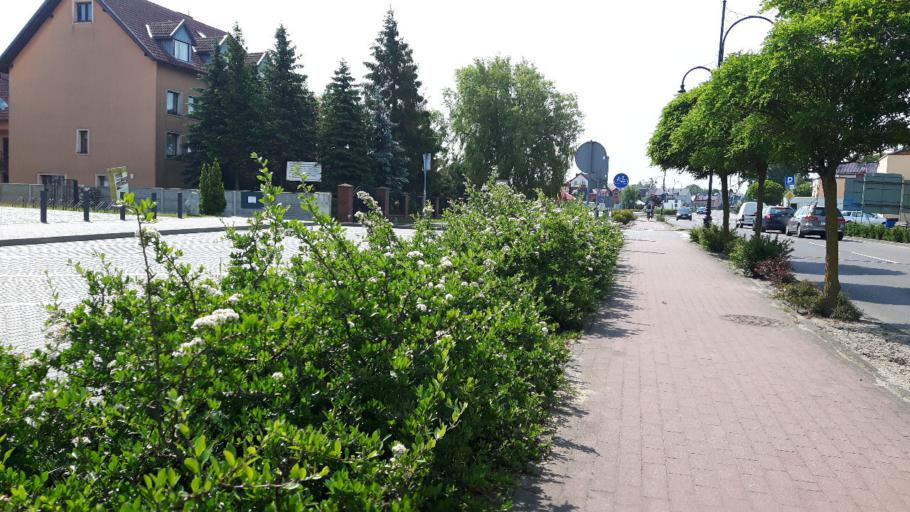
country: PL
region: Pomeranian Voivodeship
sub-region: Powiat leborski
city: Leba
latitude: 54.7555
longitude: 17.5630
